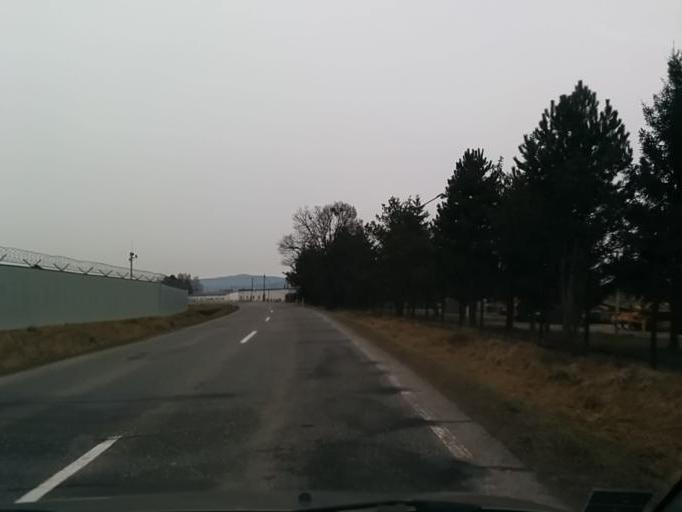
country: SK
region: Banskobystricky
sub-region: Okres Banska Bystrica
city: Zvolen
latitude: 48.6339
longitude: 19.1408
